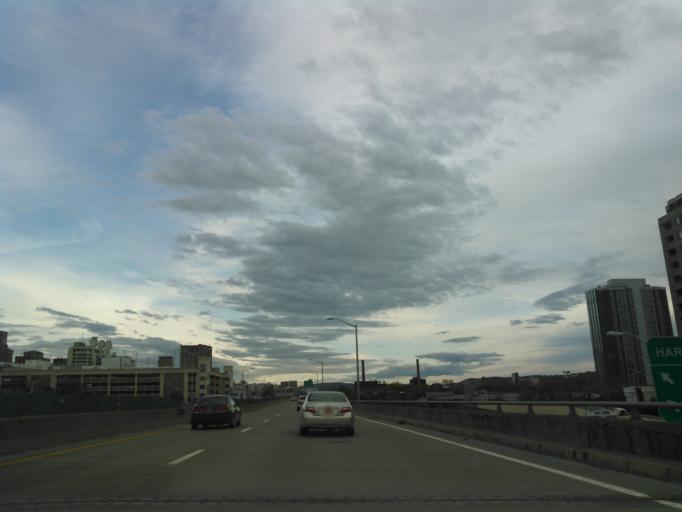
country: US
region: New York
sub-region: Onondaga County
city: Syracuse
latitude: 43.0467
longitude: -76.1427
